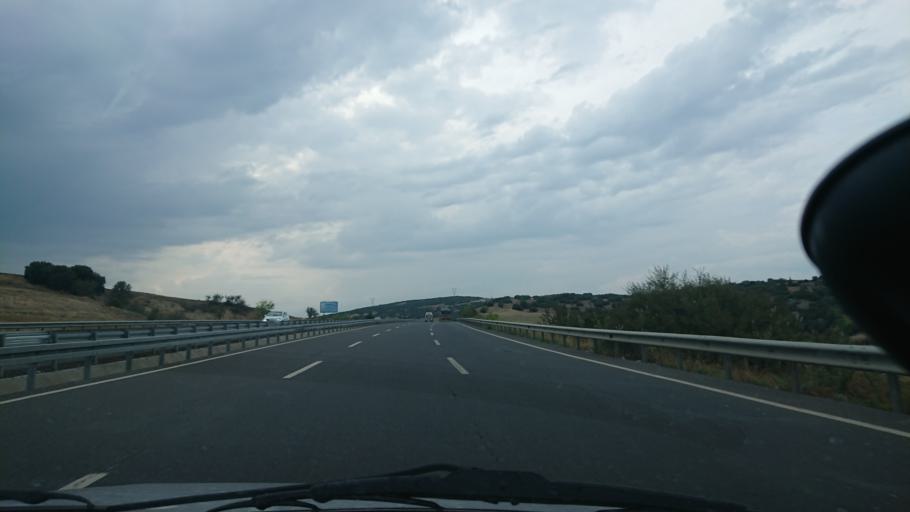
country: TR
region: Manisa
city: Selendi
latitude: 38.6189
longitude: 28.8701
